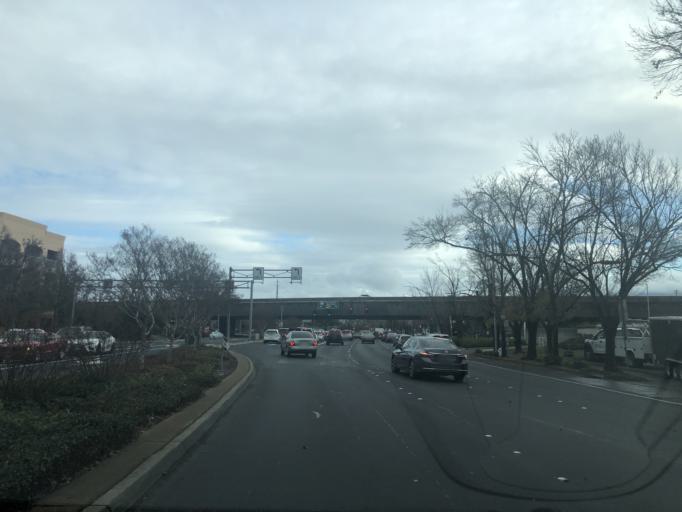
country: US
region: California
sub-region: Contra Costa County
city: Pleasant Hill
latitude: 37.9454
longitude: -122.0601
